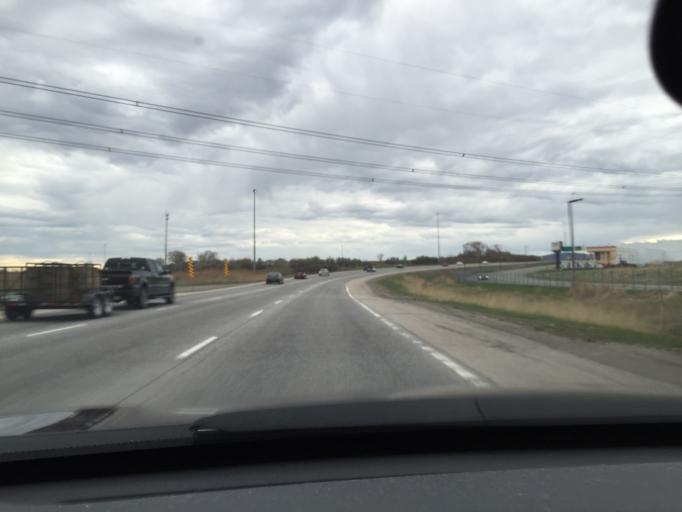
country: CA
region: Quebec
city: L'Ancienne-Lorette
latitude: 46.8152
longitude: -71.3327
